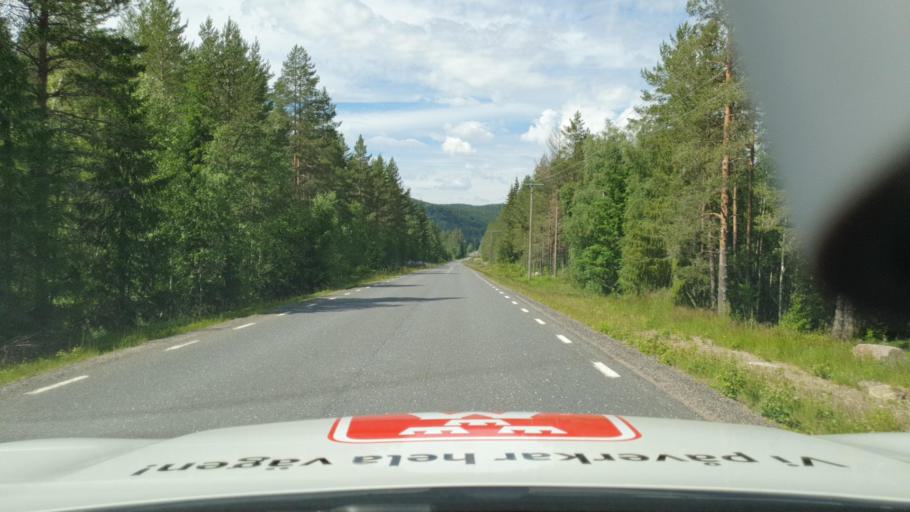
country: SE
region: Vaermland
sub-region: Torsby Kommun
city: Torsby
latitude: 60.5621
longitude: 12.7567
